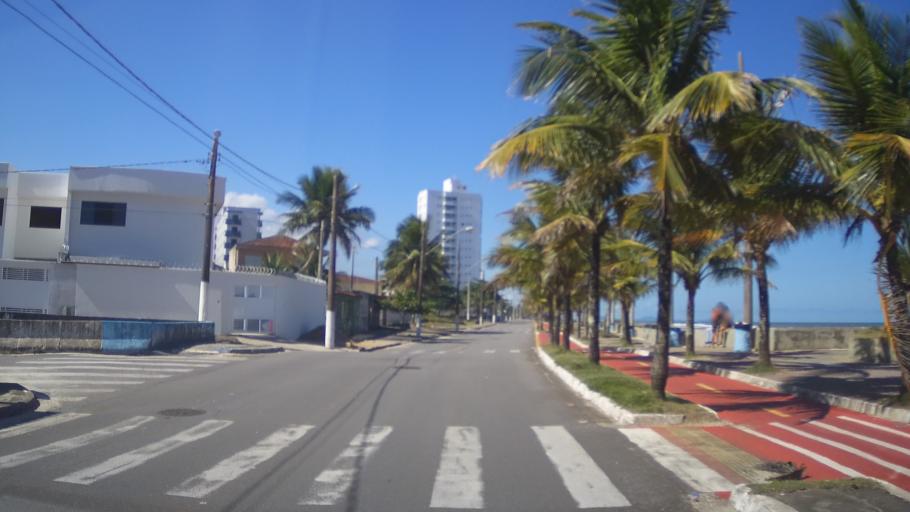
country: BR
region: Sao Paulo
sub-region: Mongagua
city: Mongagua
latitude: -24.1208
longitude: -46.6692
